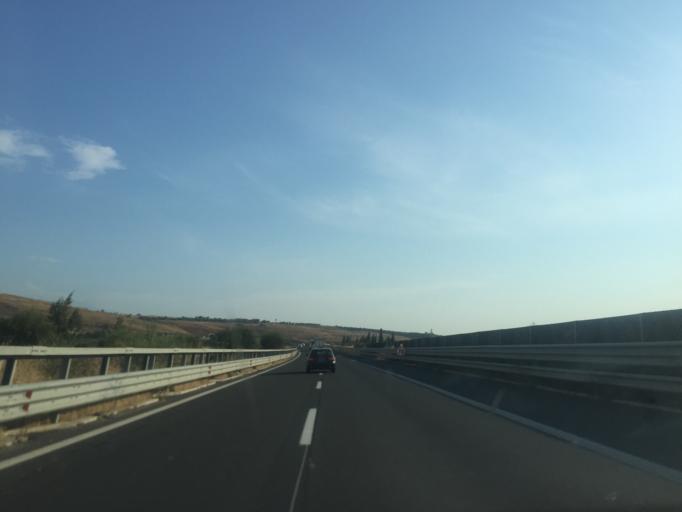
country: IT
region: Sicily
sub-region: Provincia di Siracusa
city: Carlentini
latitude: 37.3521
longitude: 15.0462
